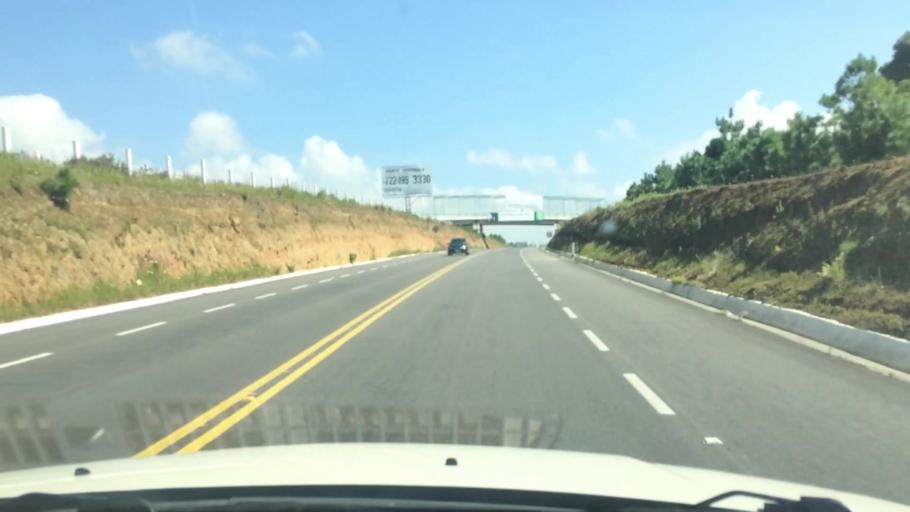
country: MX
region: Mexico
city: Amanalco de Becerra
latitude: 19.3037
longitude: -100.0099
